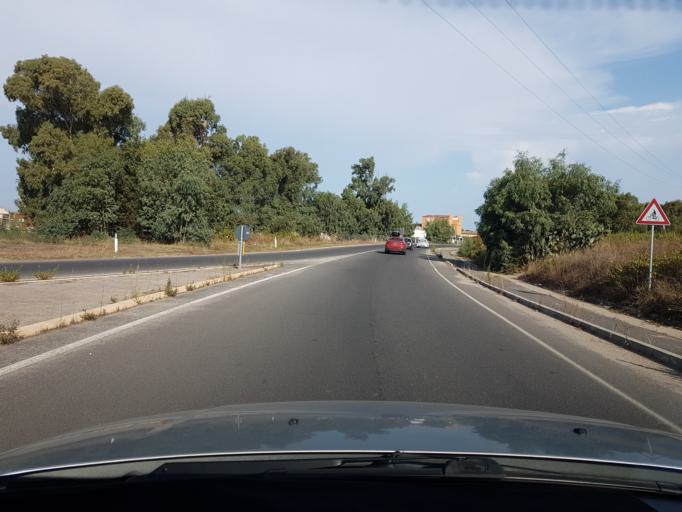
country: IT
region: Sardinia
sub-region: Provincia di Oristano
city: Cabras
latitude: 39.9147
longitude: 8.5420
